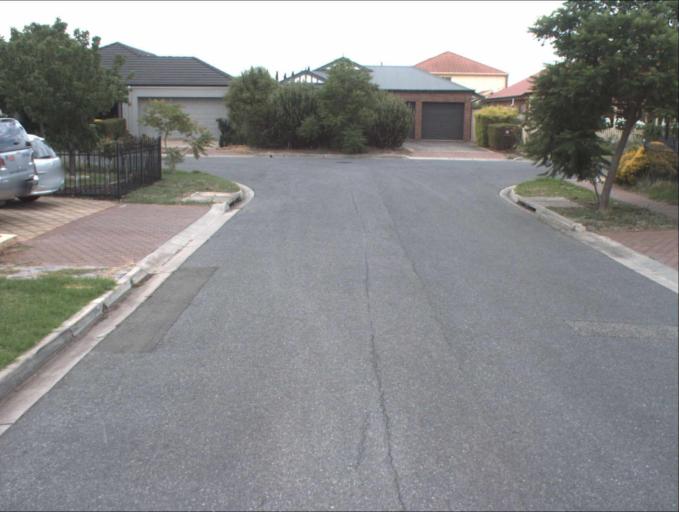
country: AU
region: South Australia
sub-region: Port Adelaide Enfield
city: Gilles Plains
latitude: -34.8557
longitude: 138.6278
